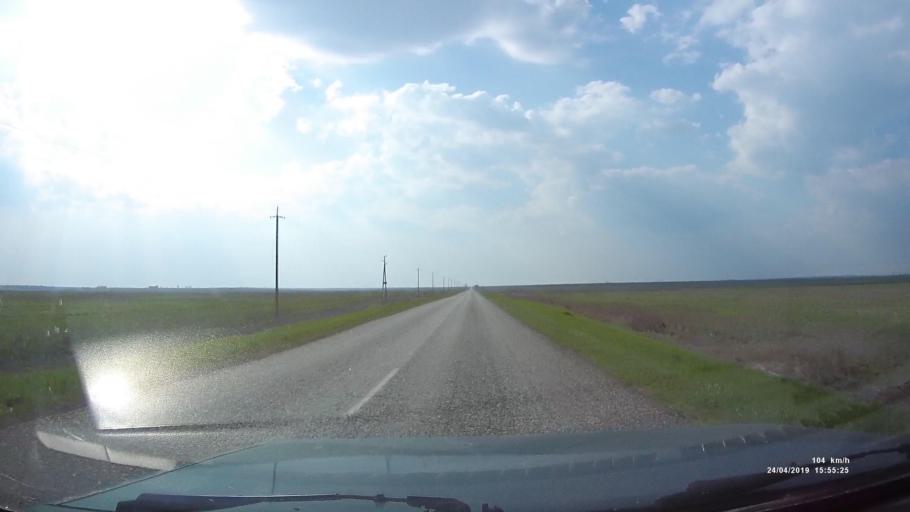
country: RU
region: Kalmykiya
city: Yashalta
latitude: 46.5902
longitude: 42.5498
